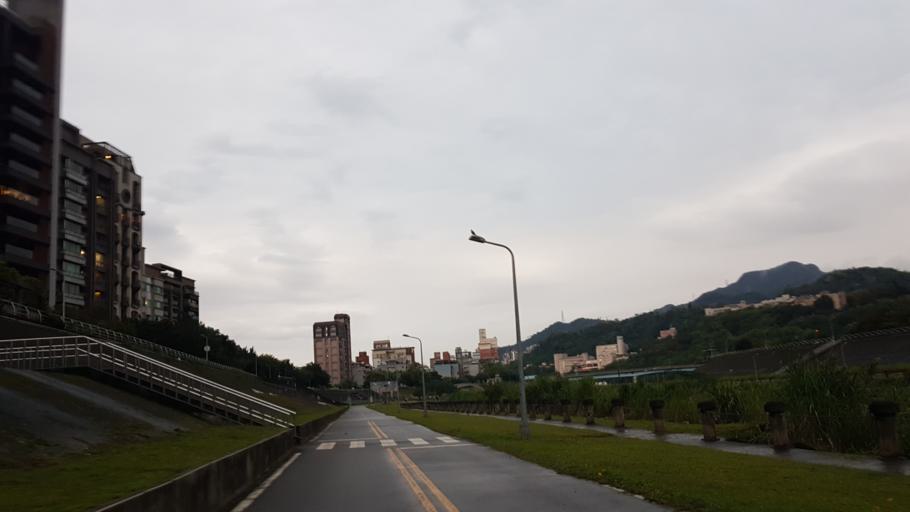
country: TW
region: Taipei
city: Taipei
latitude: 24.9804
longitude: 121.5629
